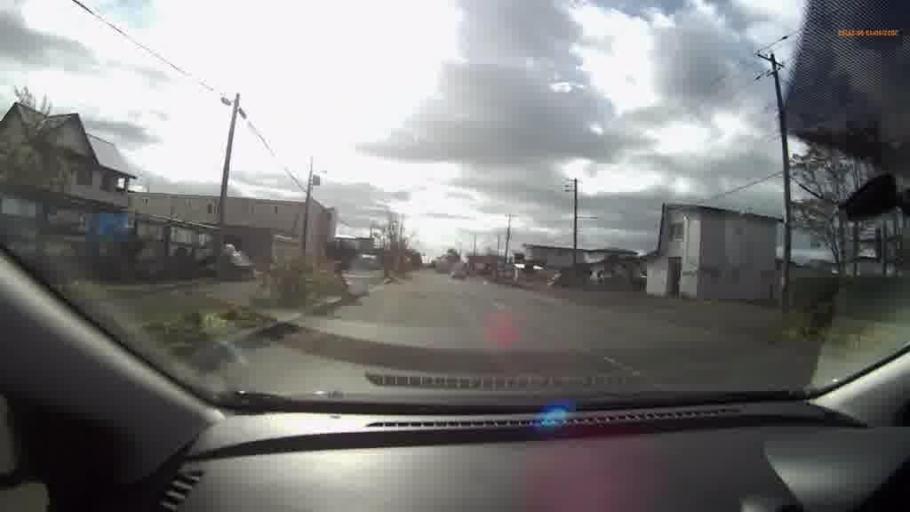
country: JP
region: Hokkaido
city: Kushiro
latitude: 42.9797
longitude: 144.1272
